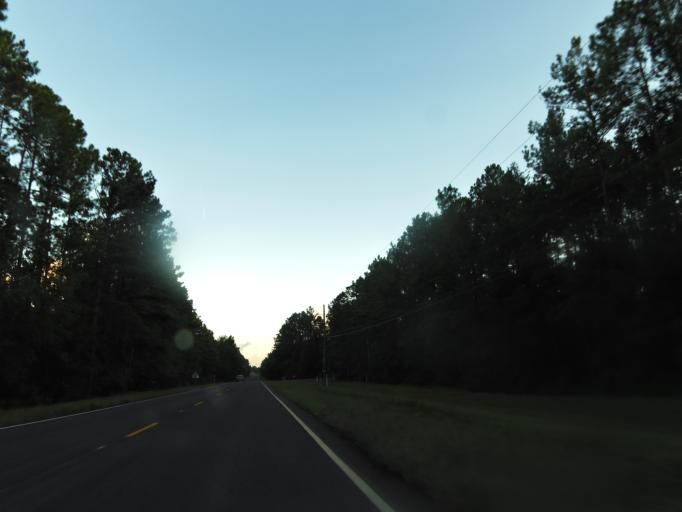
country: US
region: Georgia
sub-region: Camden County
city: Woodbine
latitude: 30.9862
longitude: -81.7286
